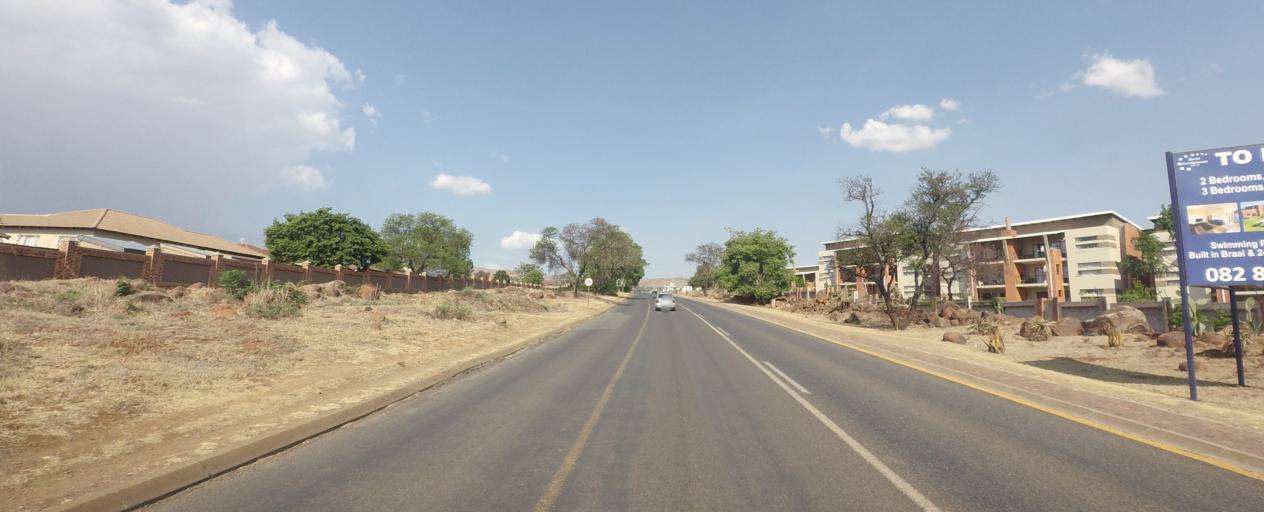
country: ZA
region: Mpumalanga
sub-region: Ehlanzeni District
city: Lydenburg
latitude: -25.1027
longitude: 30.4746
